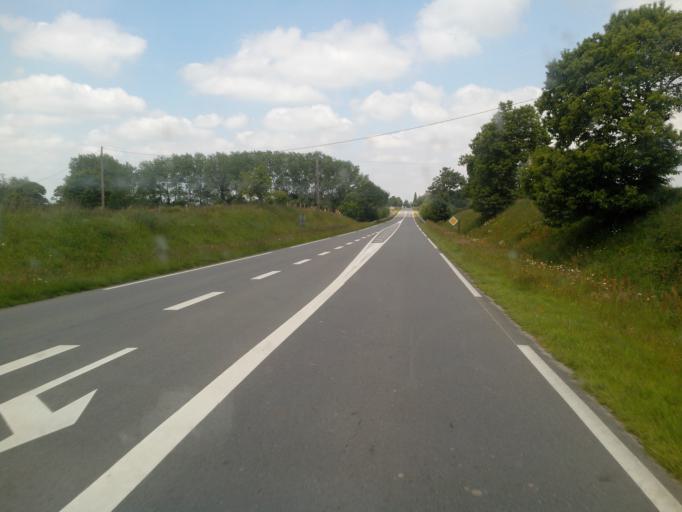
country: FR
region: Brittany
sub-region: Departement d'Ille-et-Vilaine
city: Saint-Germain-en-Cogles
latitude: 48.3866
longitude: -1.2748
